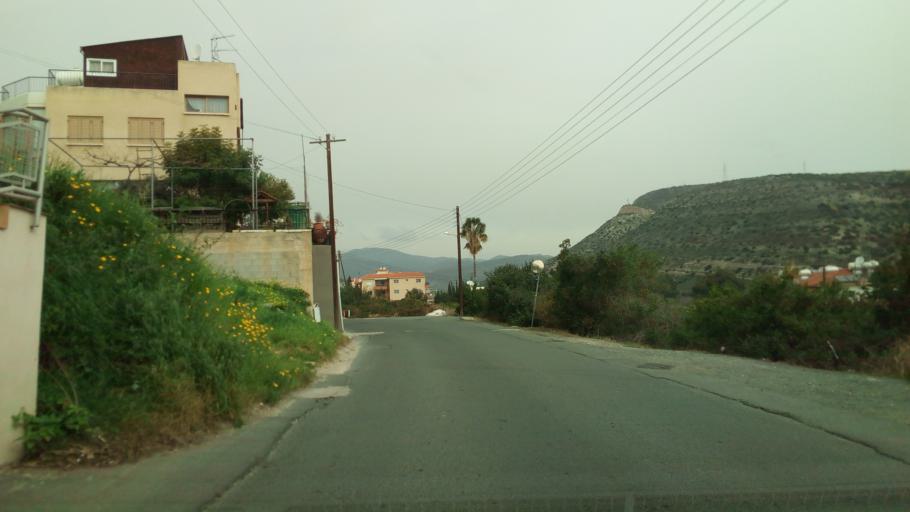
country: CY
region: Limassol
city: Mouttagiaka
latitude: 34.7252
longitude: 33.0846
